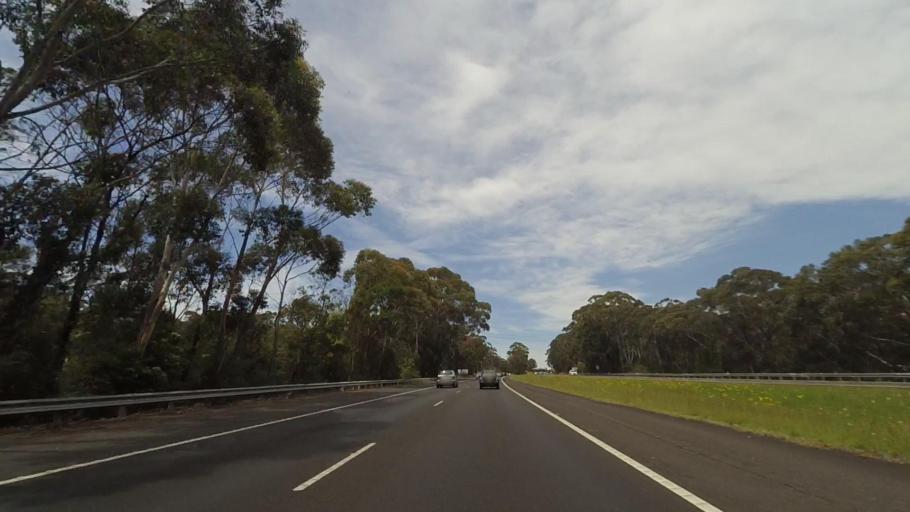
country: AU
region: New South Wales
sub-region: Wollongong
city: Helensburgh
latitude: -34.2011
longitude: 150.9657
